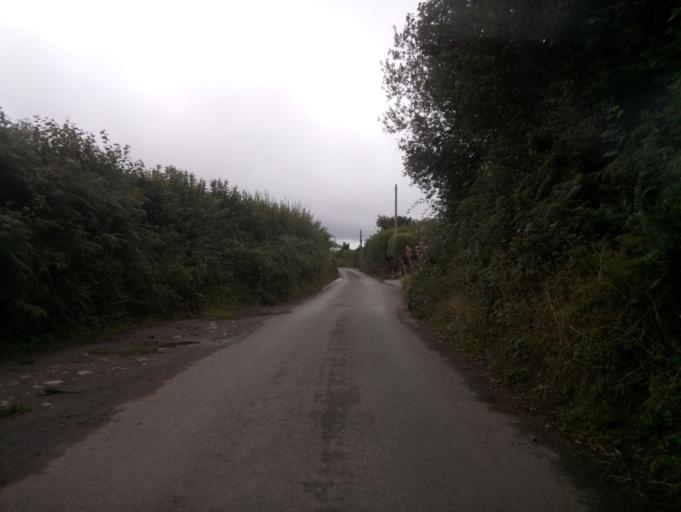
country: GB
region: England
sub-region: Devon
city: Kingsbridge
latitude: 50.3078
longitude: -3.7163
